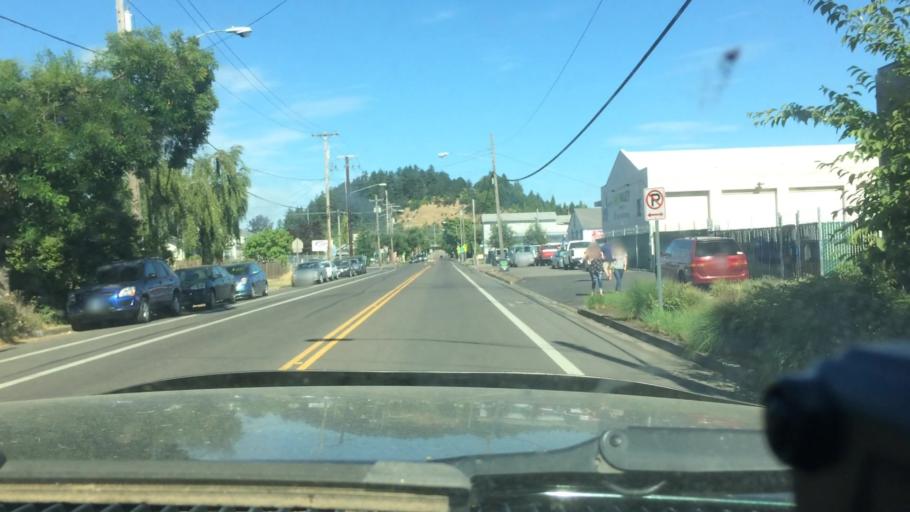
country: US
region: Oregon
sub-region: Lane County
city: Eugene
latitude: 44.0587
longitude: -123.1075
